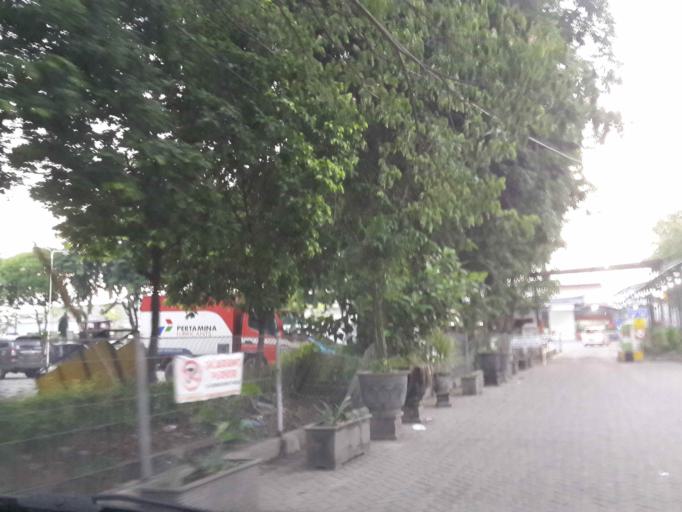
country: ID
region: East Java
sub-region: Kota Surabaya
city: Surabaya
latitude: -7.2487
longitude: 112.7321
